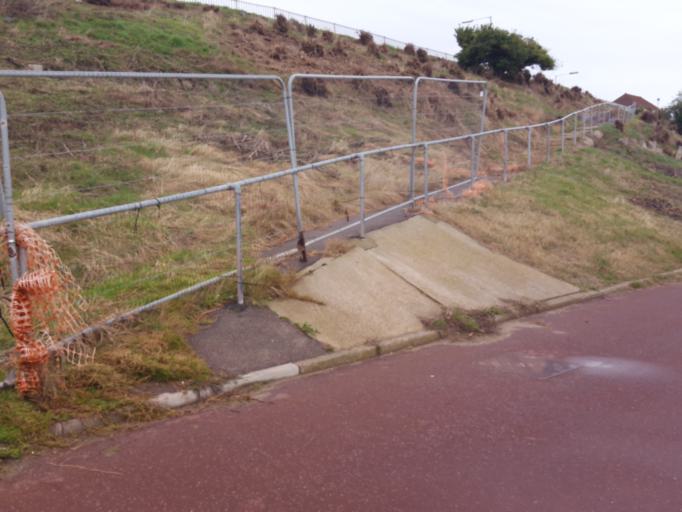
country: GB
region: England
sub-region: Essex
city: Clacton-on-Sea
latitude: 51.7975
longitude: 1.1840
